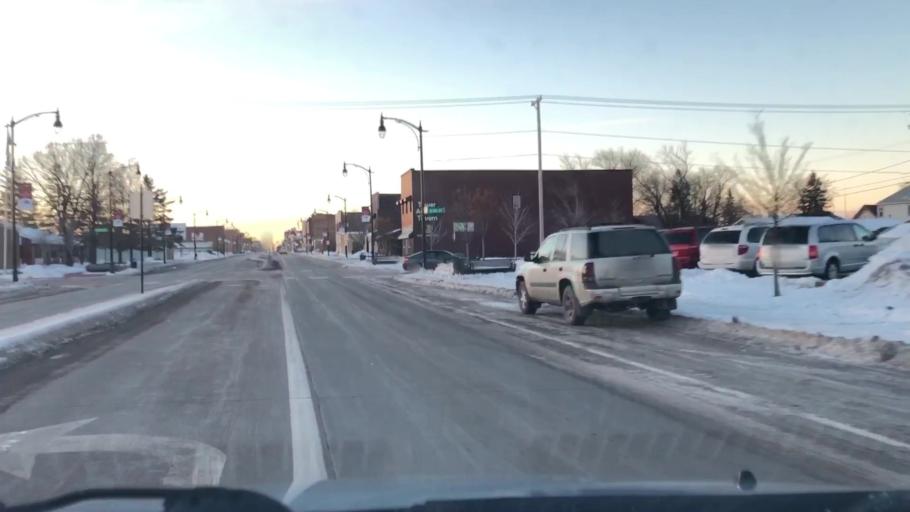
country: US
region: Wisconsin
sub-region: Douglas County
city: Superior
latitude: 46.7343
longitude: -92.1039
